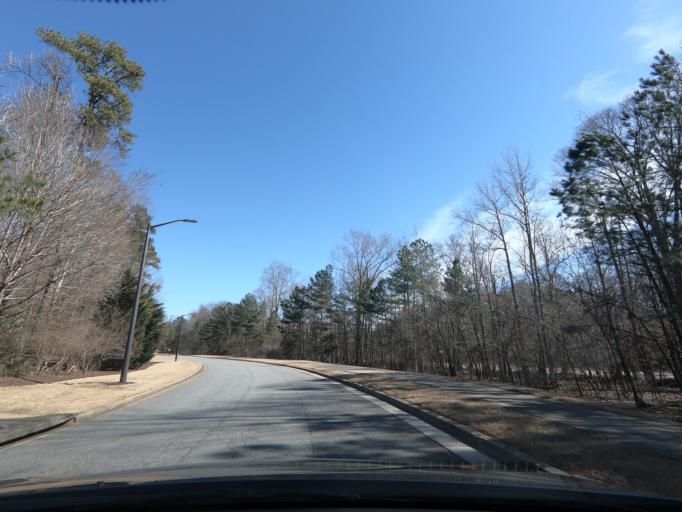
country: US
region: Georgia
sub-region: Cobb County
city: Kennesaw
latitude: 34.0523
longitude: -84.6373
